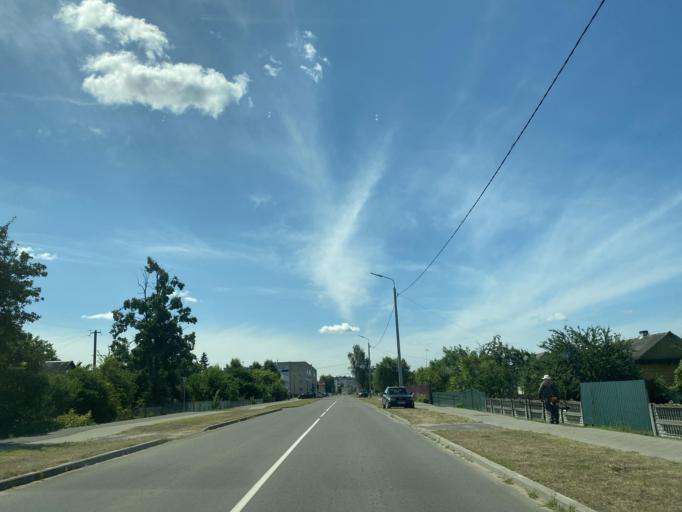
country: BY
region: Brest
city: Ivanava
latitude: 52.1537
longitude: 25.5436
